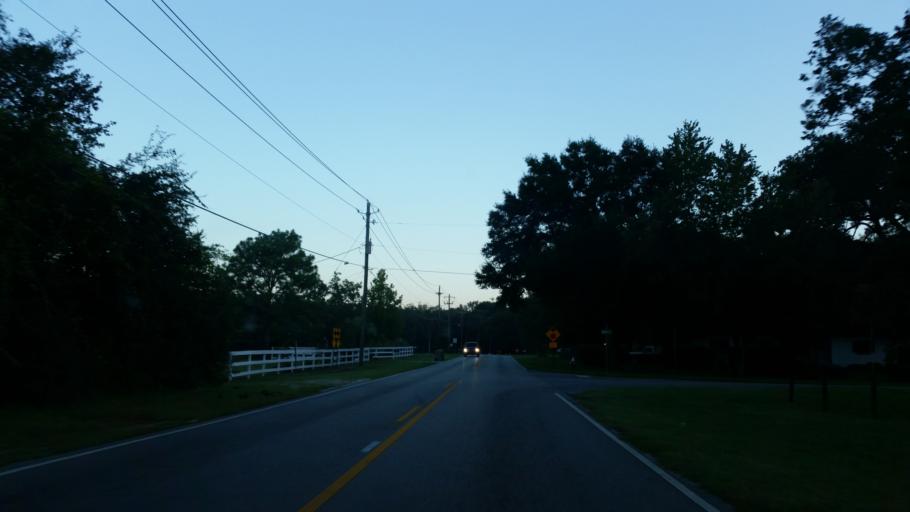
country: US
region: Florida
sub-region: Escambia County
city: Bellview
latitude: 30.4471
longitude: -87.3115
